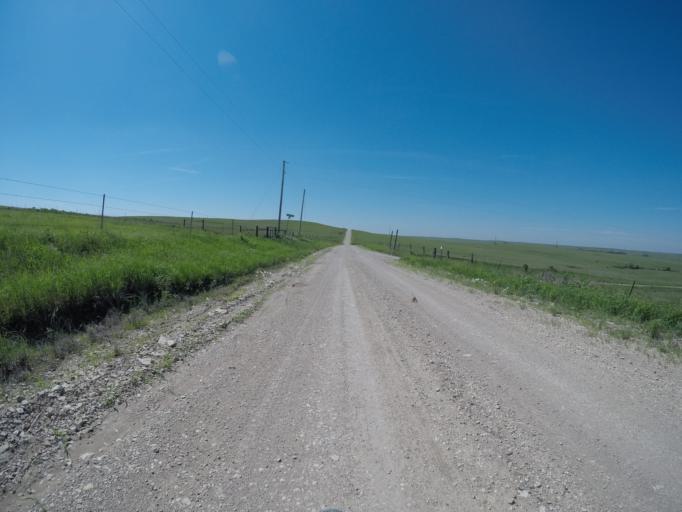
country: US
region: Kansas
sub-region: Wabaunsee County
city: Alma
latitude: 39.0009
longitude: -96.1783
